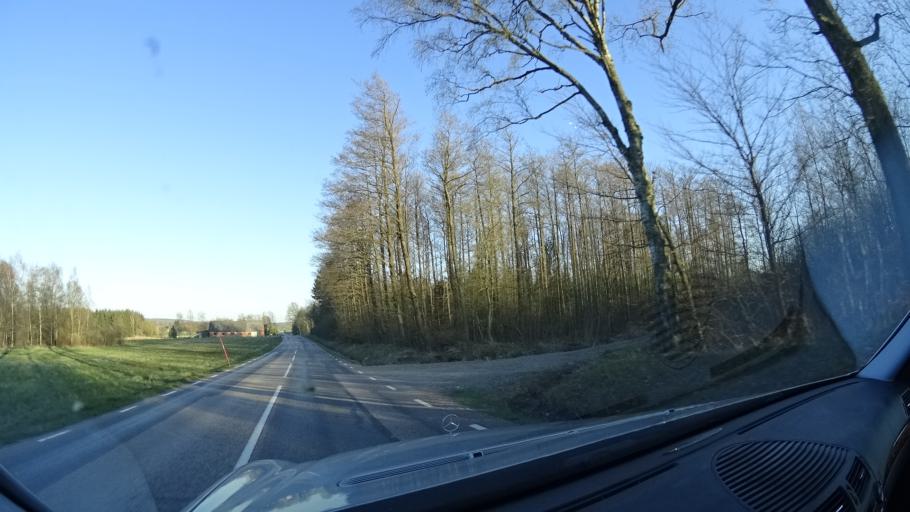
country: SE
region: Skane
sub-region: Bjuvs Kommun
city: Billesholm
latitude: 56.0307
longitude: 13.0362
